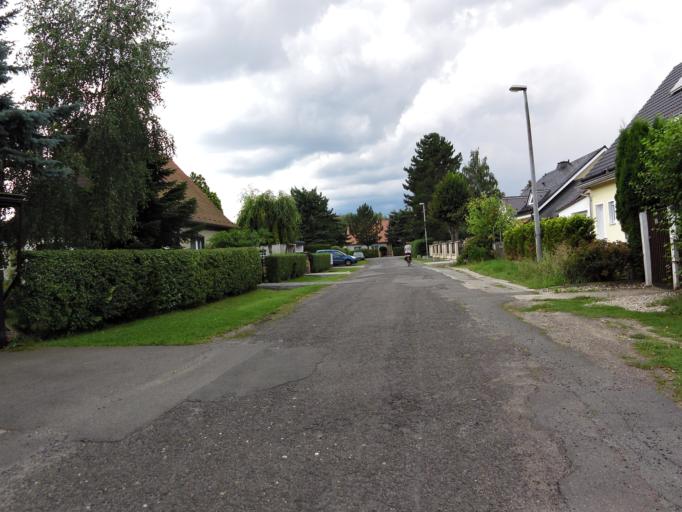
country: DE
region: Saxony
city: Rackwitz
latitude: 51.3849
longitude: 12.4021
